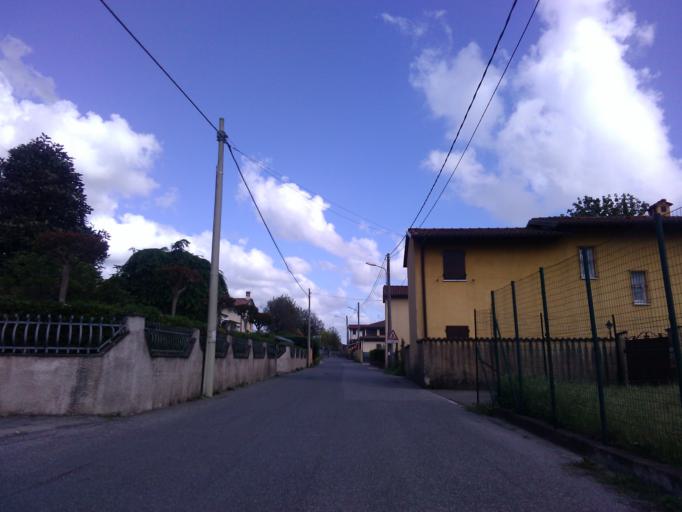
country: IT
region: Tuscany
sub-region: Provincia di Massa-Carrara
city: Capanne-Prato-Cinquale
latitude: 44.0055
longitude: 10.1499
